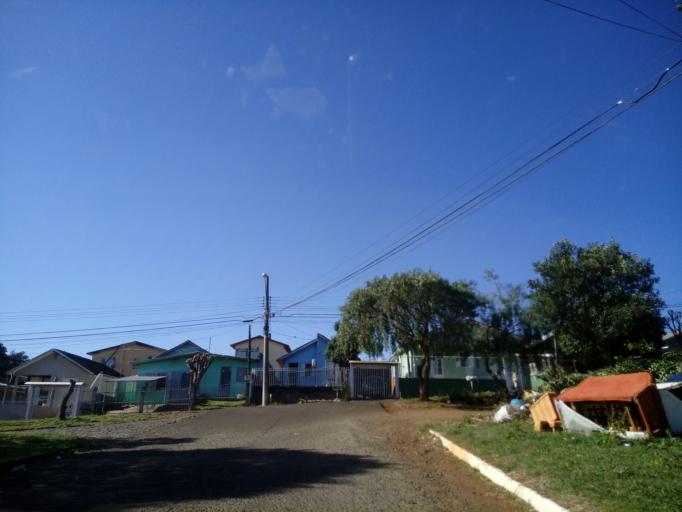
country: BR
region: Santa Catarina
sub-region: Chapeco
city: Chapeco
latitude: -27.0829
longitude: -52.6326
